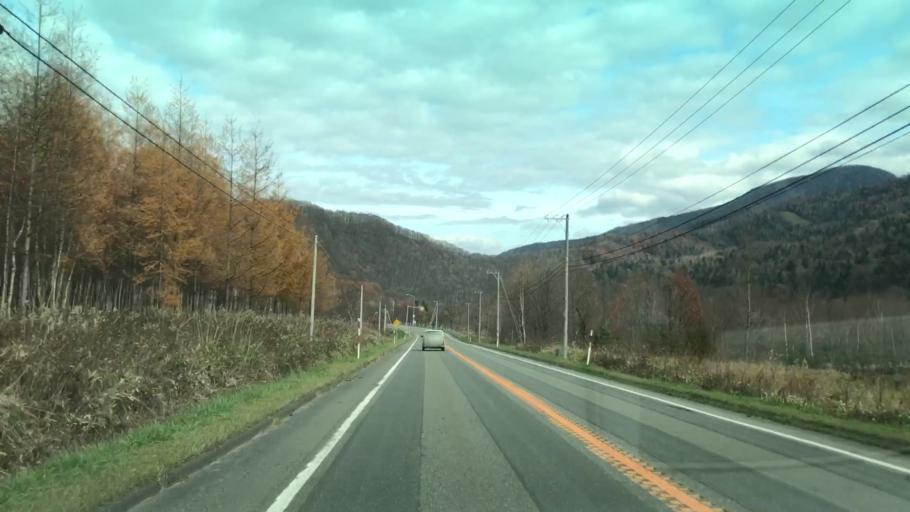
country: JP
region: Hokkaido
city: Shizunai-furukawacho
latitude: 42.7821
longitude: 142.3927
